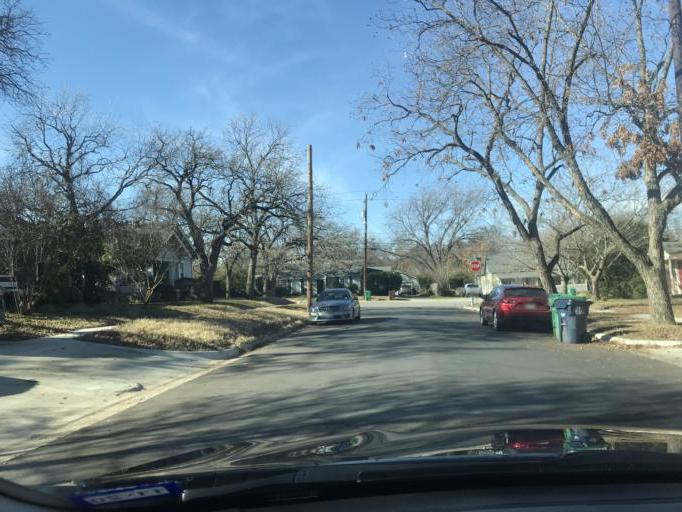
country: US
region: Texas
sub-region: Denton County
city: Denton
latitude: 33.2205
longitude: -97.1494
